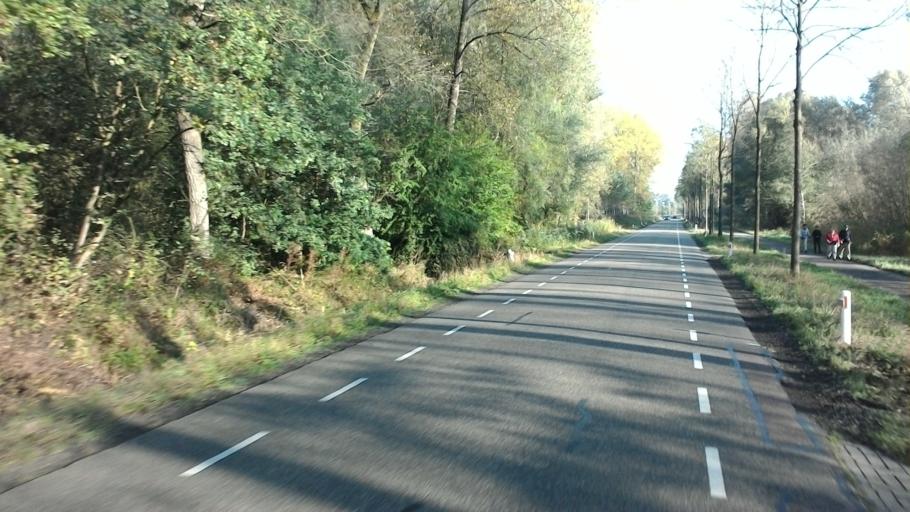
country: NL
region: North Brabant
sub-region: Gemeente Schijndel
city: Schijndel
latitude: 51.6371
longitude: 5.4592
